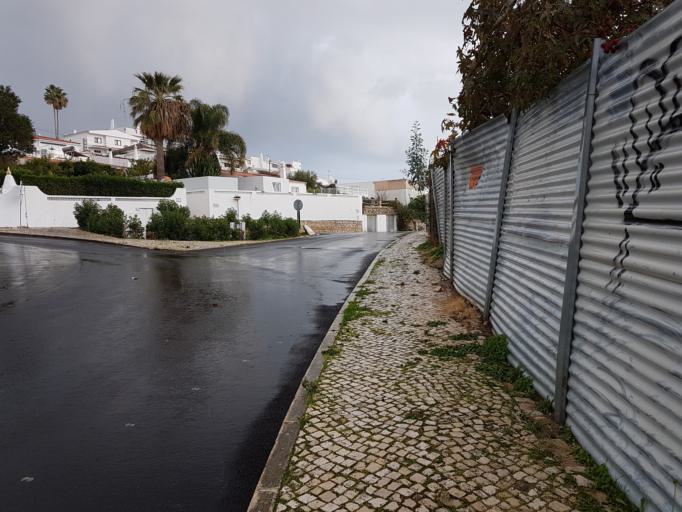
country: PT
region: Faro
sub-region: Albufeira
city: Albufeira
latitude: 37.0865
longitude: -8.2621
